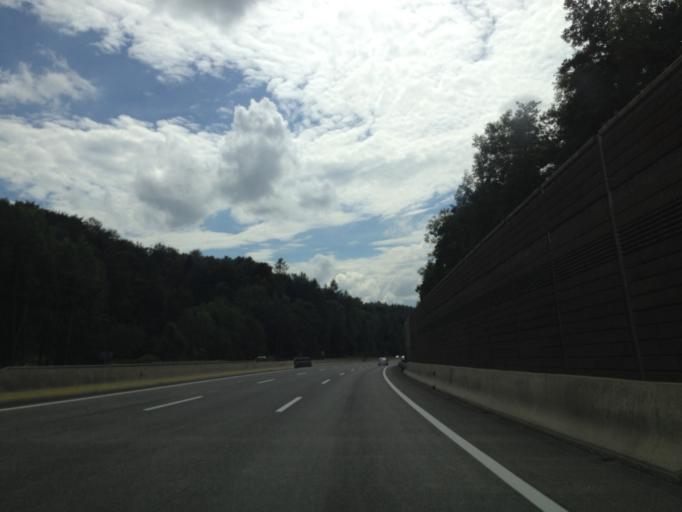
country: AT
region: Styria
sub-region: Politischer Bezirk Graz-Umgebung
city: Hart bei Graz
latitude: 47.0598
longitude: 15.5532
